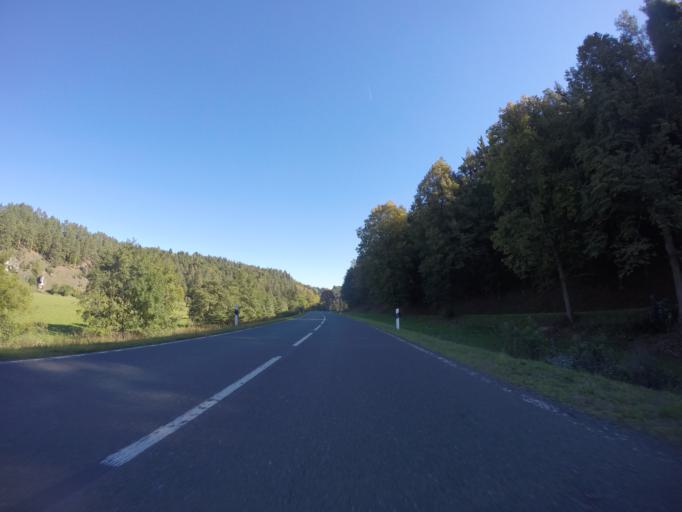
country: DE
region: Bavaria
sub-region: Upper Franconia
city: Waischenfeld
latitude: 49.8113
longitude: 11.3583
